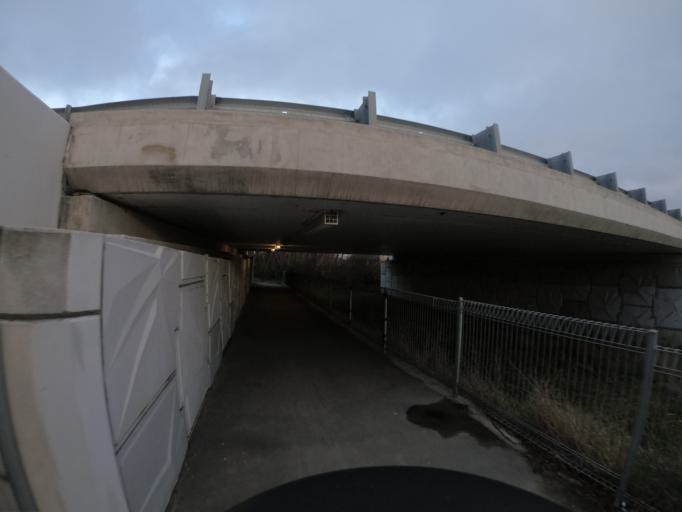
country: NZ
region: Canterbury
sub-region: Selwyn District
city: Prebbleton
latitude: -43.5610
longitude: 172.5612
